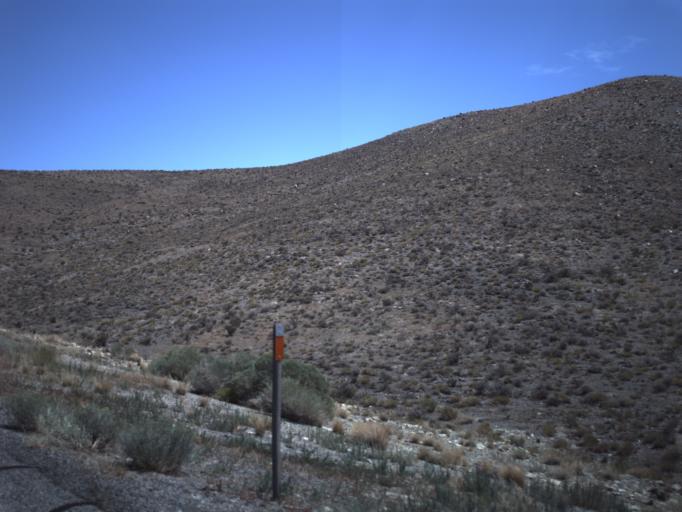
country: US
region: Utah
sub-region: Beaver County
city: Milford
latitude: 39.0275
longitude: -113.3455
